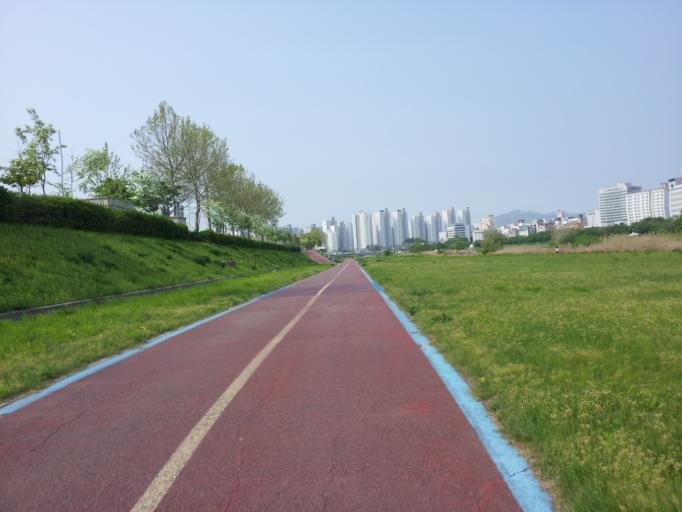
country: KR
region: Daejeon
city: Daejeon
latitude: 36.3561
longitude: 127.3560
